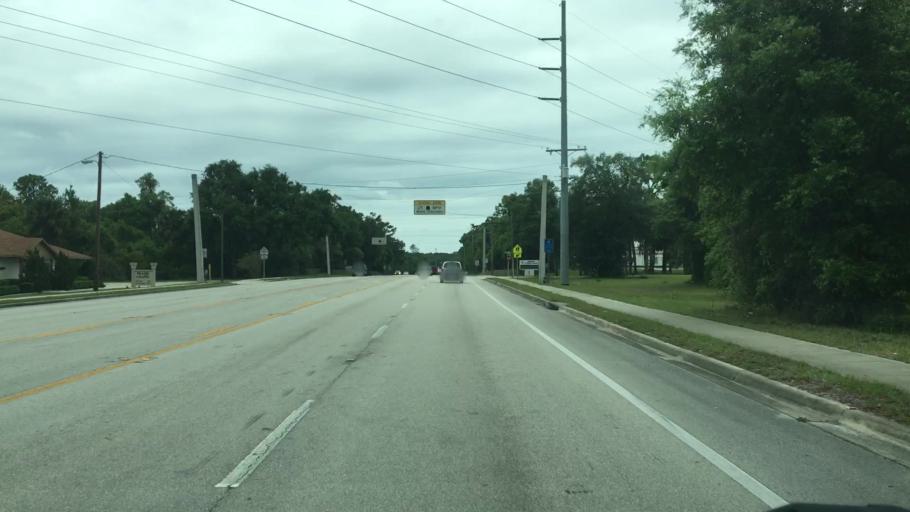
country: US
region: Florida
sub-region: Volusia County
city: De Land Southwest
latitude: 29.0054
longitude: -81.3172
